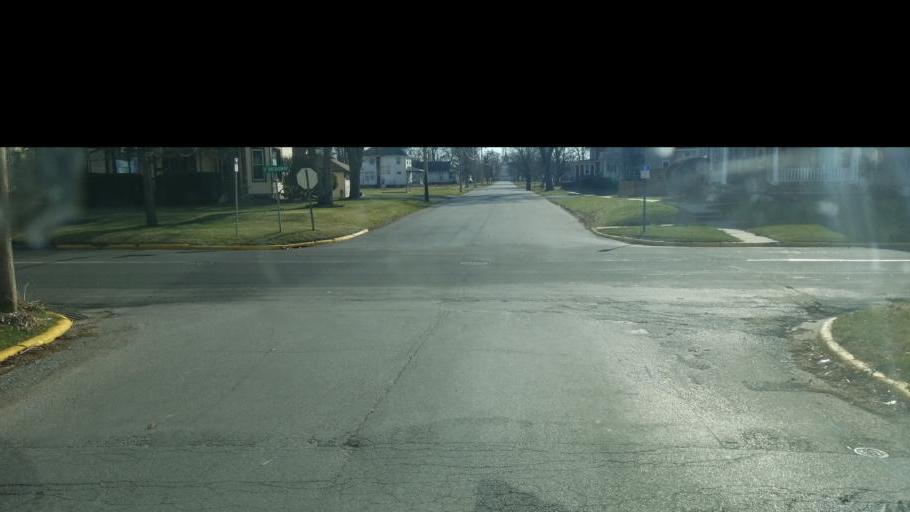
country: US
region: Illinois
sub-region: Warren County
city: Monmouth
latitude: 40.9124
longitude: -90.6570
